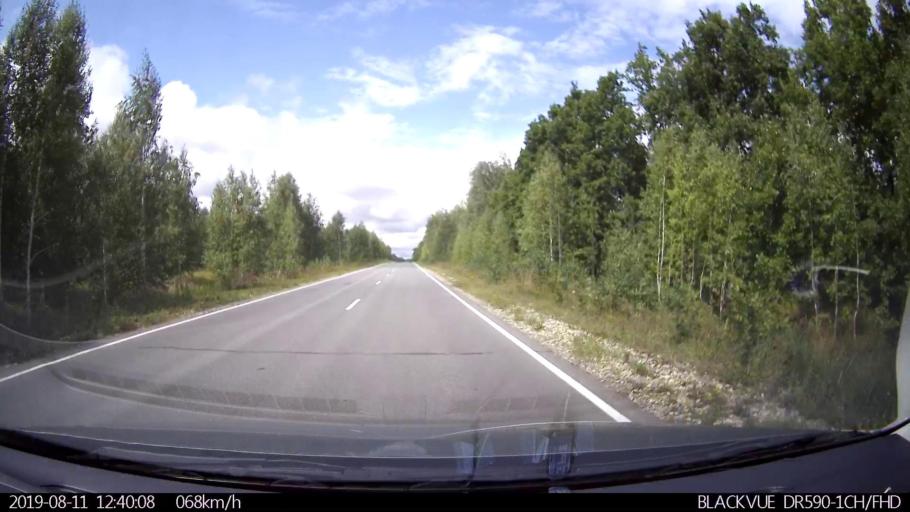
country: RU
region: Ulyanovsk
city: Ignatovka
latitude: 53.8369
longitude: 47.7854
